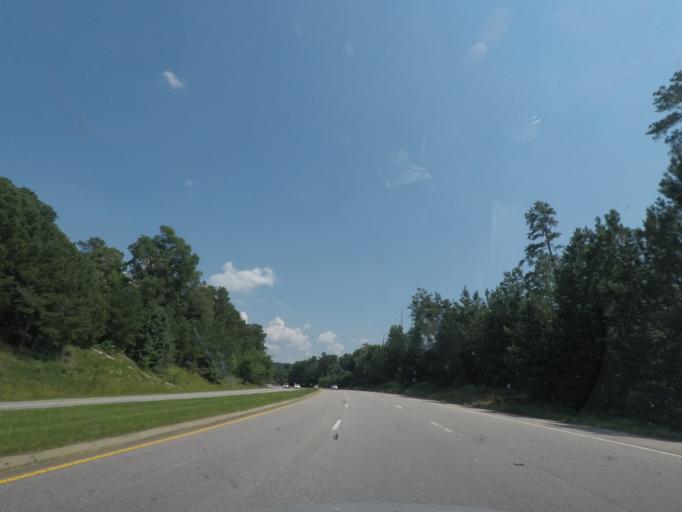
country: US
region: North Carolina
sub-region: Durham County
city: Durham
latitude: 35.9641
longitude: -78.9642
